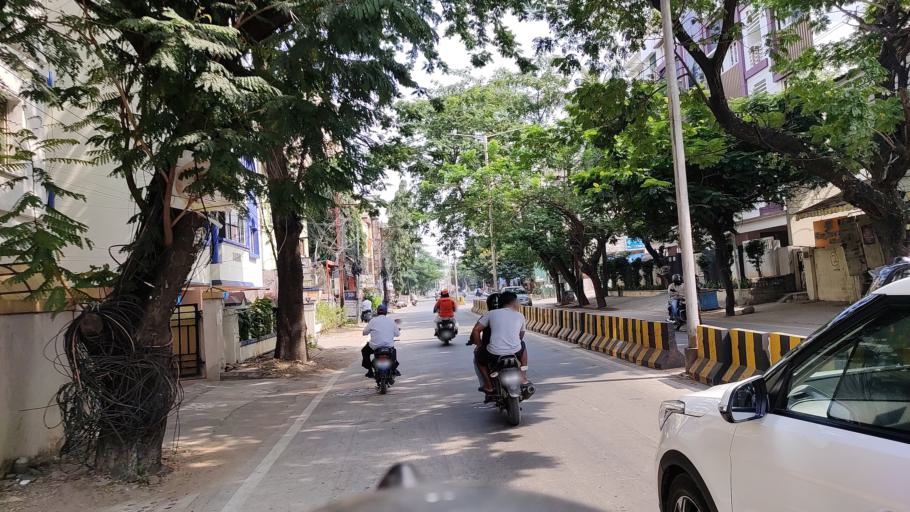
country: IN
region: Telangana
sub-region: Hyderabad
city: Hyderabad
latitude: 17.4301
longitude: 78.4449
